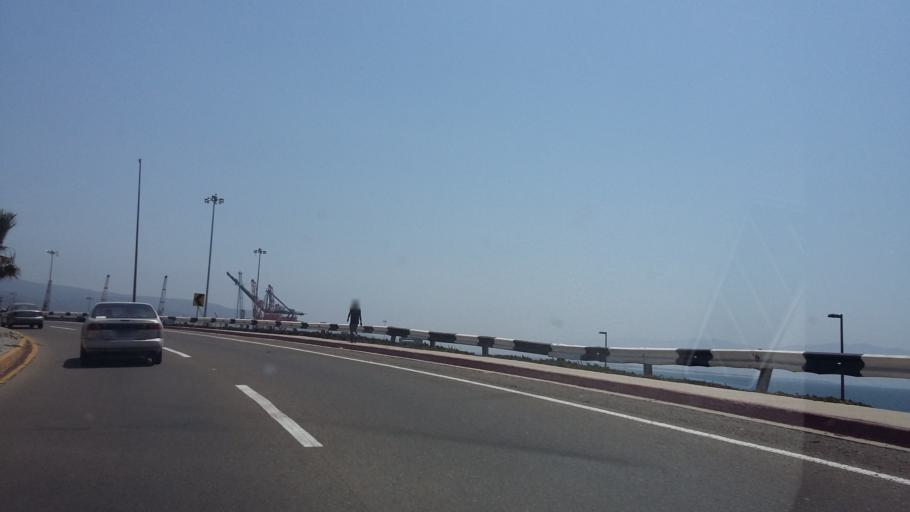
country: MX
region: Baja California
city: Ensenada
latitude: 31.8584
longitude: -116.6374
